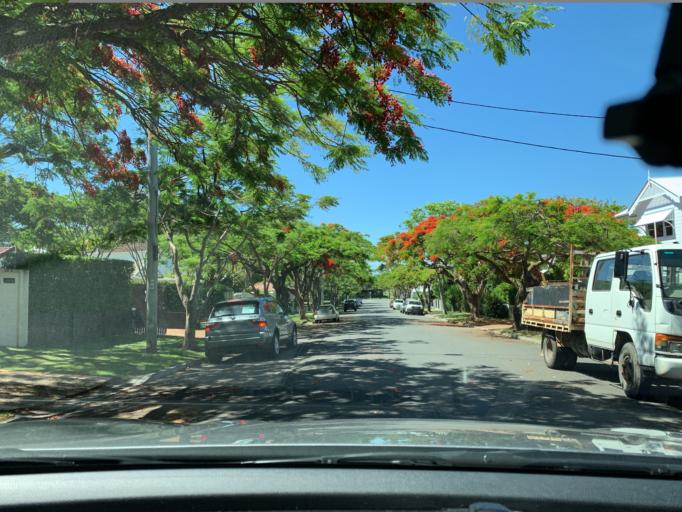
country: AU
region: Queensland
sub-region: Brisbane
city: Ascot
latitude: -27.4205
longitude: 153.0693
